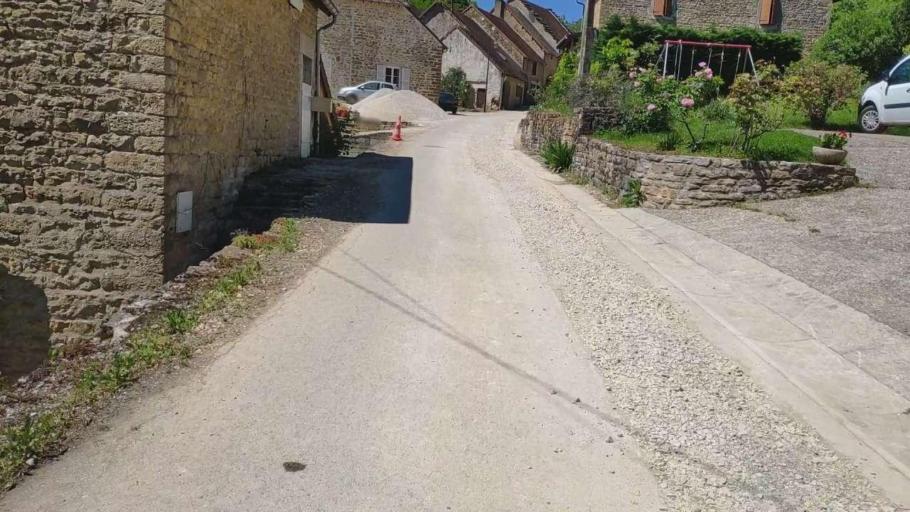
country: FR
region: Franche-Comte
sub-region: Departement du Jura
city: Perrigny
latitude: 46.7414
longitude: 5.6322
